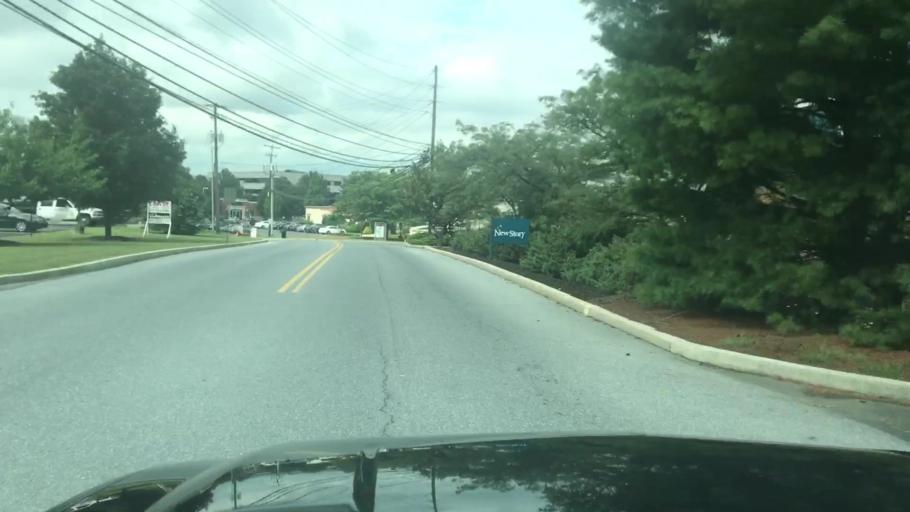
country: US
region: Pennsylvania
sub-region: Dauphin County
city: Progress
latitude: 40.3111
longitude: -76.8413
